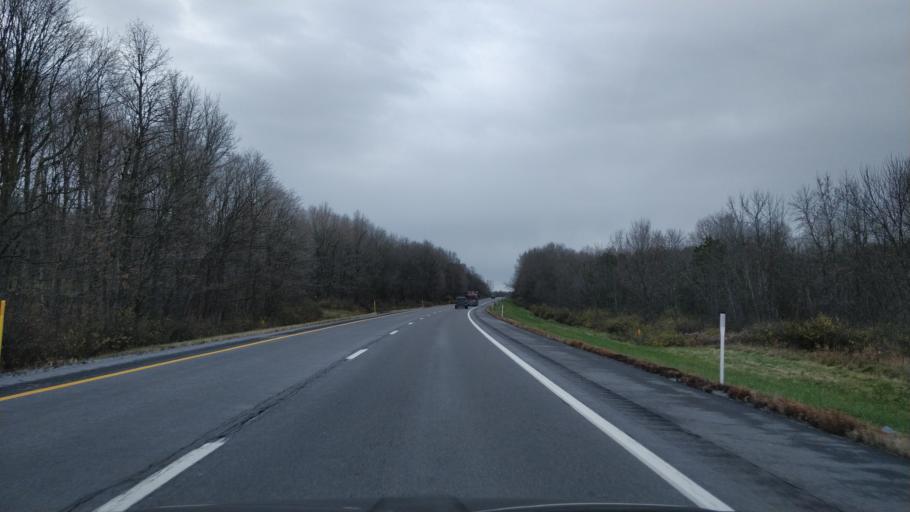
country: US
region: New York
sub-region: Jefferson County
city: Calcium
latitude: 44.1190
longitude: -75.8875
